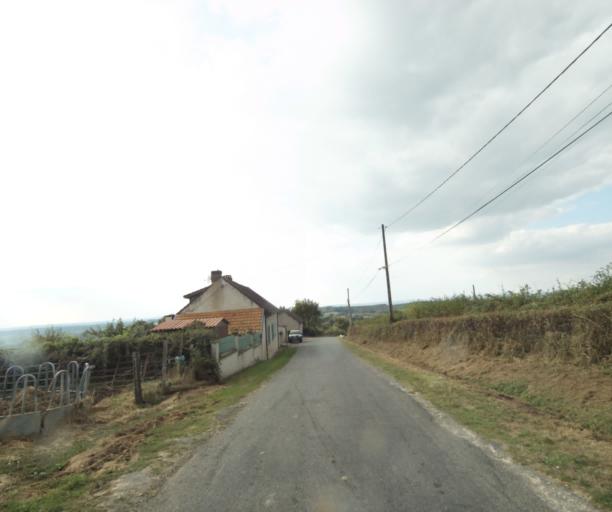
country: FR
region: Bourgogne
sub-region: Departement de Saone-et-Loire
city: Palinges
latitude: 46.5265
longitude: 4.2843
